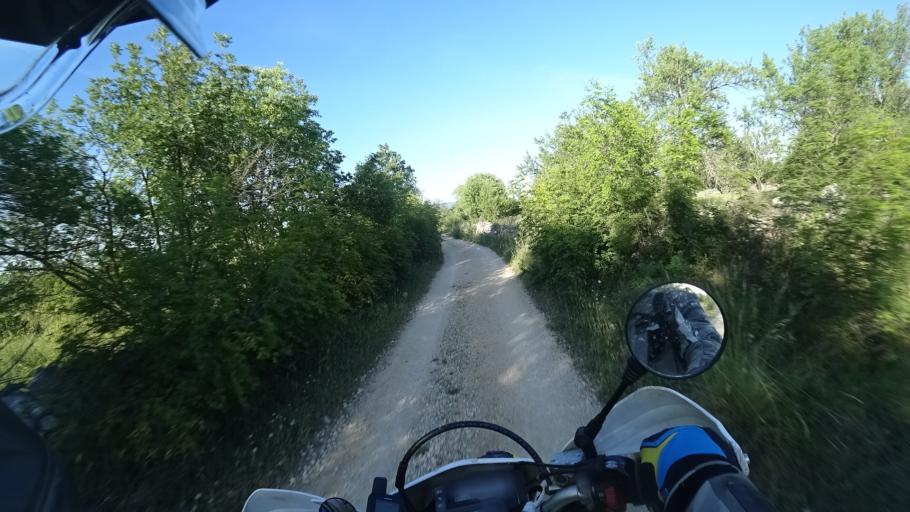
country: HR
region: Sibensko-Kniniska
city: Drnis
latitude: 43.8407
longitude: 16.0267
